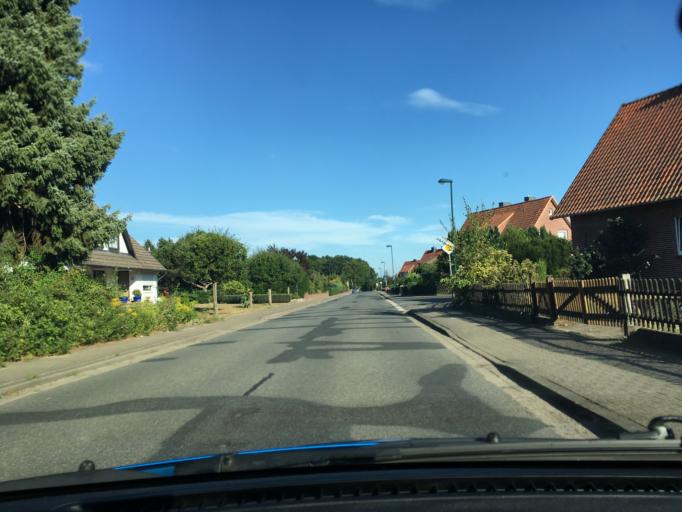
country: DE
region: Lower Saxony
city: Dahlenburg
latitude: 53.1909
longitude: 10.7269
